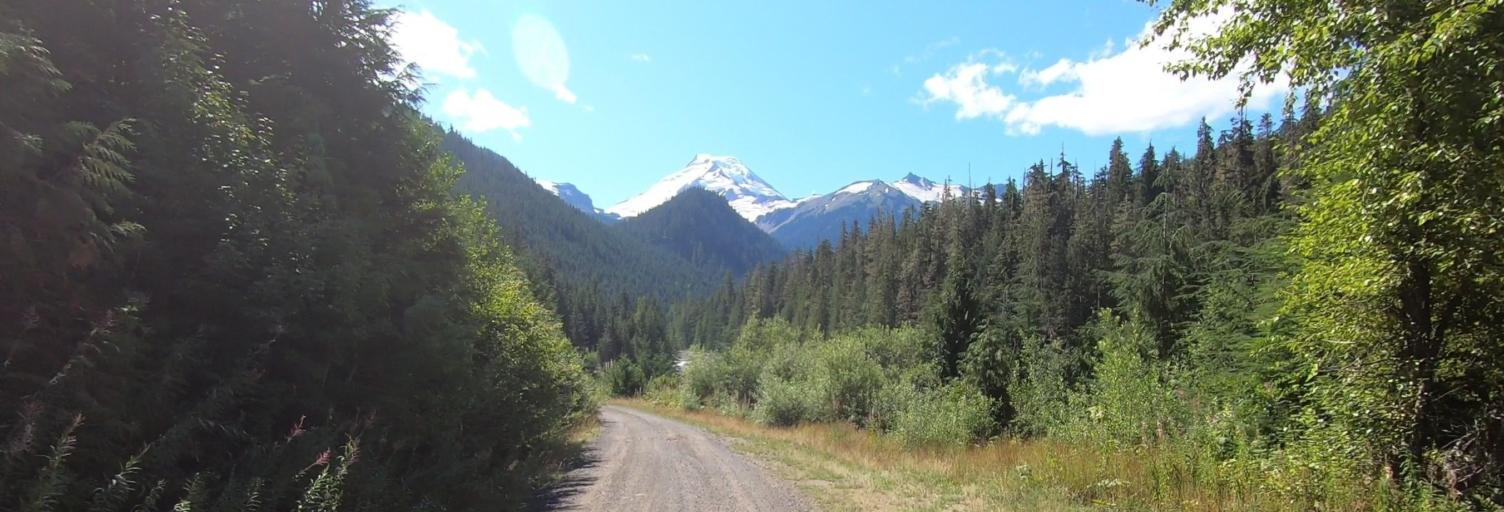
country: CA
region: British Columbia
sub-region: Fraser Valley Regional District
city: Chilliwack
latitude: 48.8696
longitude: -121.7661
